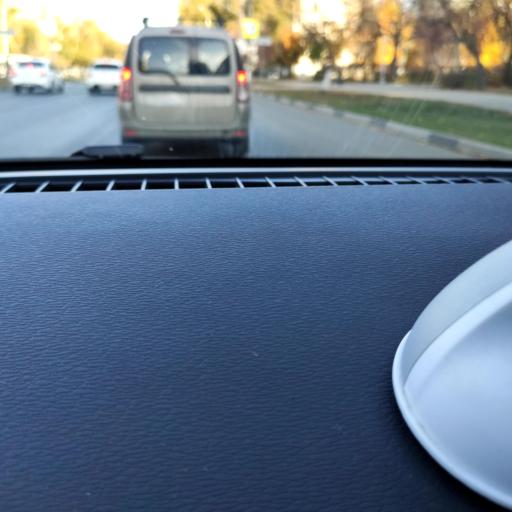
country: RU
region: Samara
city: Samara
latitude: 53.2004
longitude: 50.1833
